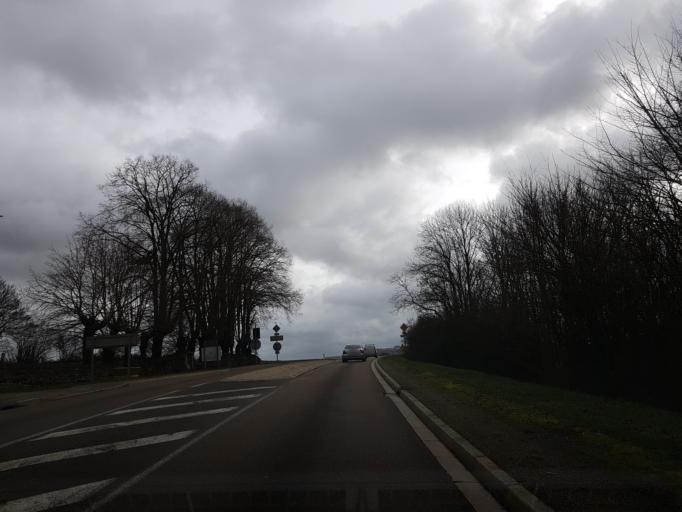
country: FR
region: Champagne-Ardenne
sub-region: Departement de la Haute-Marne
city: Langres
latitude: 47.9004
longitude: 5.3069
